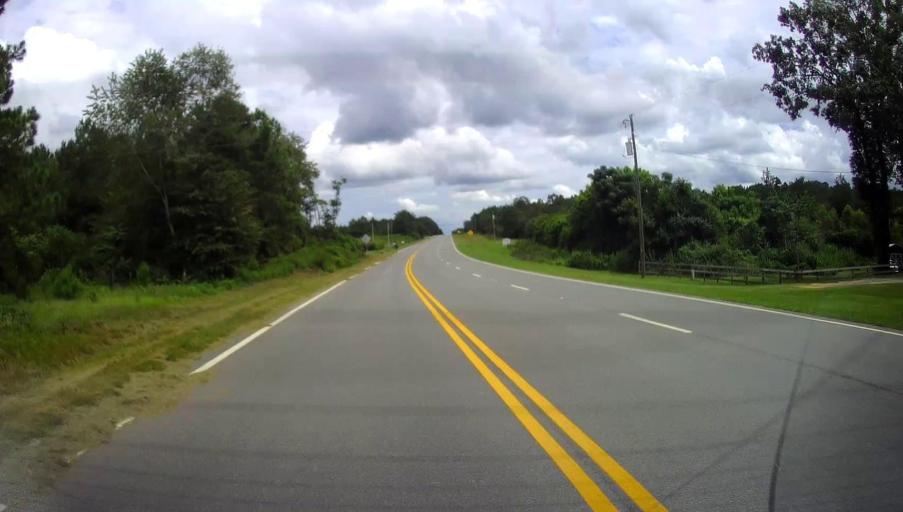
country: US
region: Georgia
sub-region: Macon County
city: Oglethorpe
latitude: 32.2817
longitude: -84.1457
